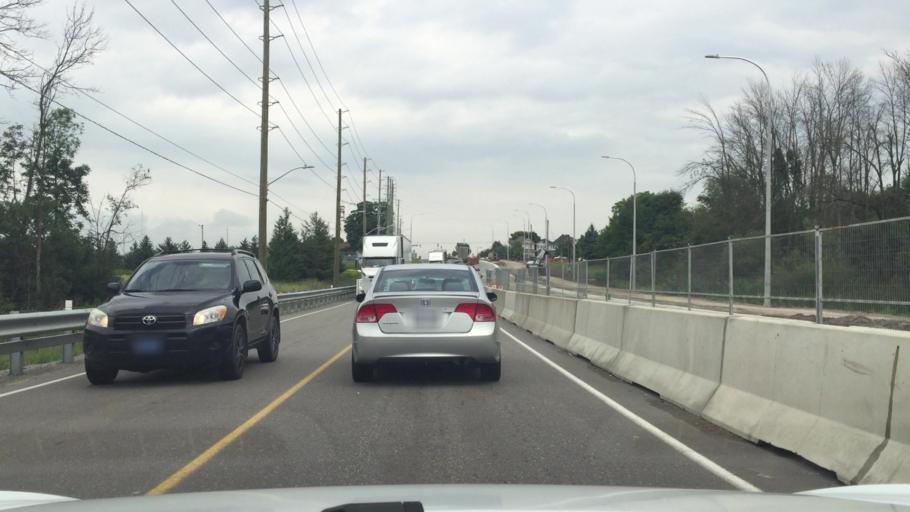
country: CA
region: Ontario
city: Ajax
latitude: 43.8571
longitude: -78.9591
